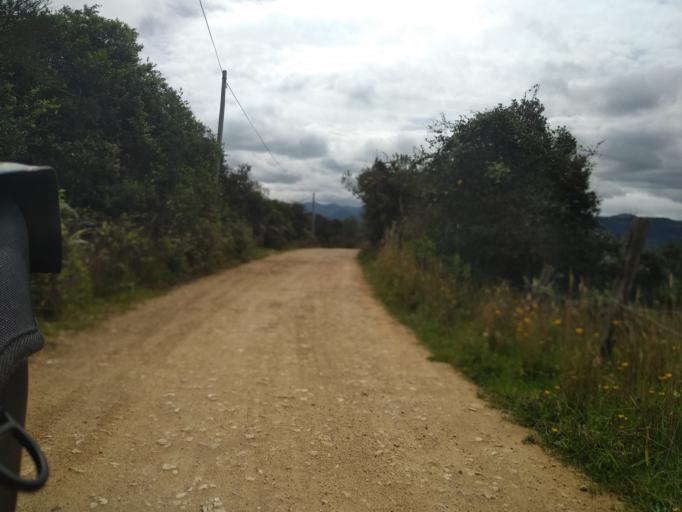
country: CO
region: Cundinamarca
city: Lenguazaque
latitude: 5.2840
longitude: -73.7411
